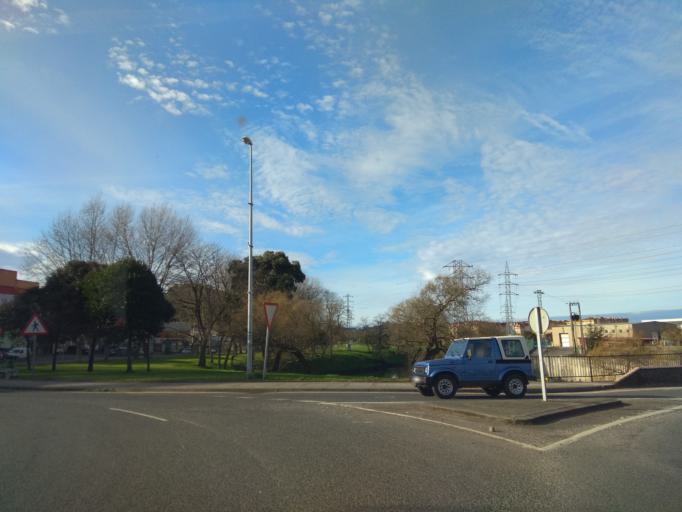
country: ES
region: Cantabria
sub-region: Provincia de Cantabria
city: El Astillero
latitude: 43.4121
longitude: -3.8433
